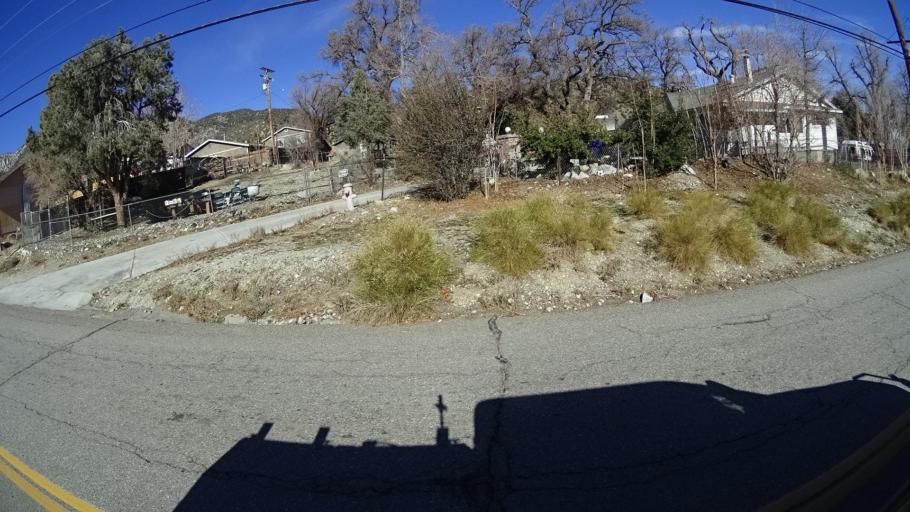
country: US
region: California
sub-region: Kern County
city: Frazier Park
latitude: 34.8200
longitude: -118.9371
